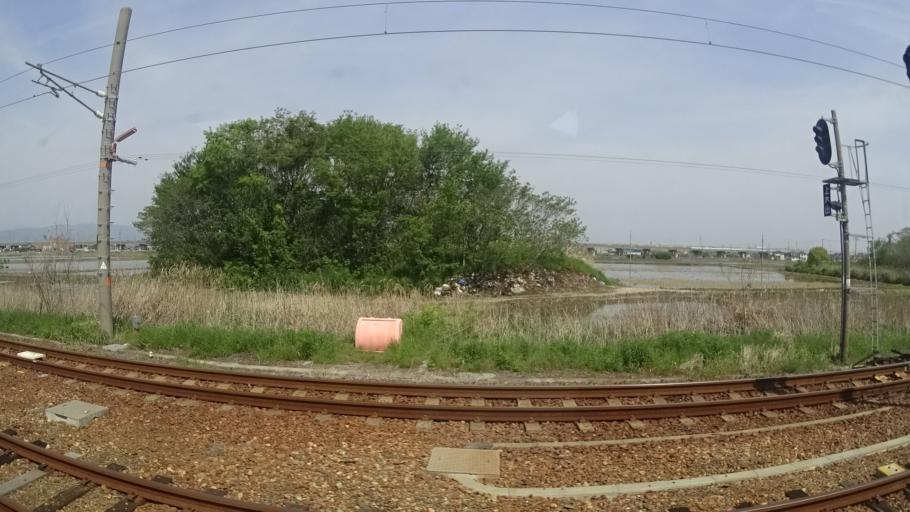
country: JP
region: Aichi
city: Kanie
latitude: 35.1339
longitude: 136.7665
